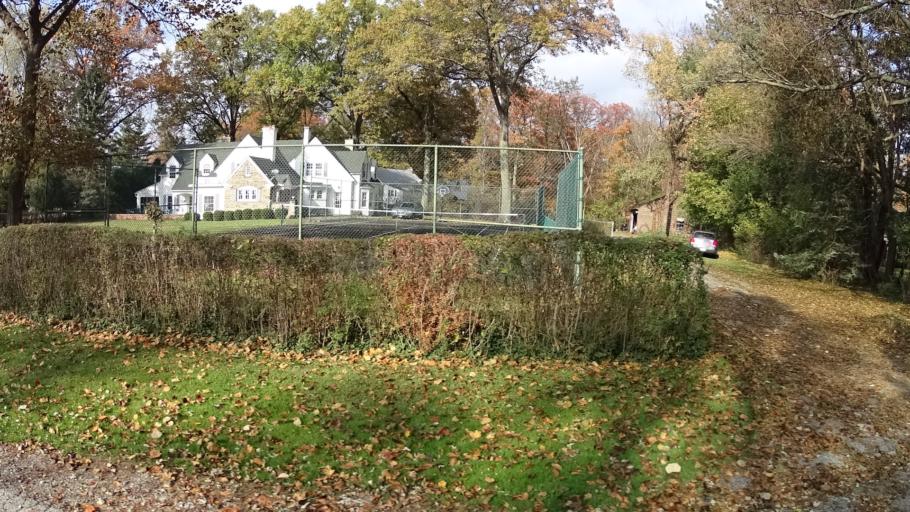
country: US
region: Ohio
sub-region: Lorain County
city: Elyria
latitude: 41.3852
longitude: -82.0992
